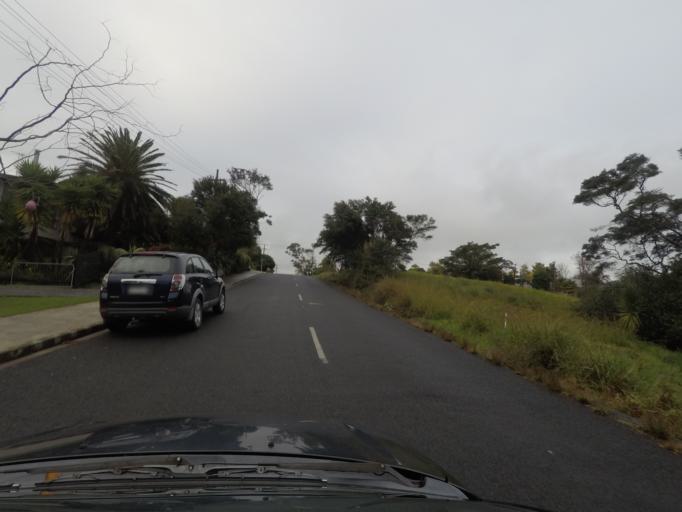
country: NZ
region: Auckland
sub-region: Auckland
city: Rosebank
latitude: -36.7613
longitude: 174.5929
